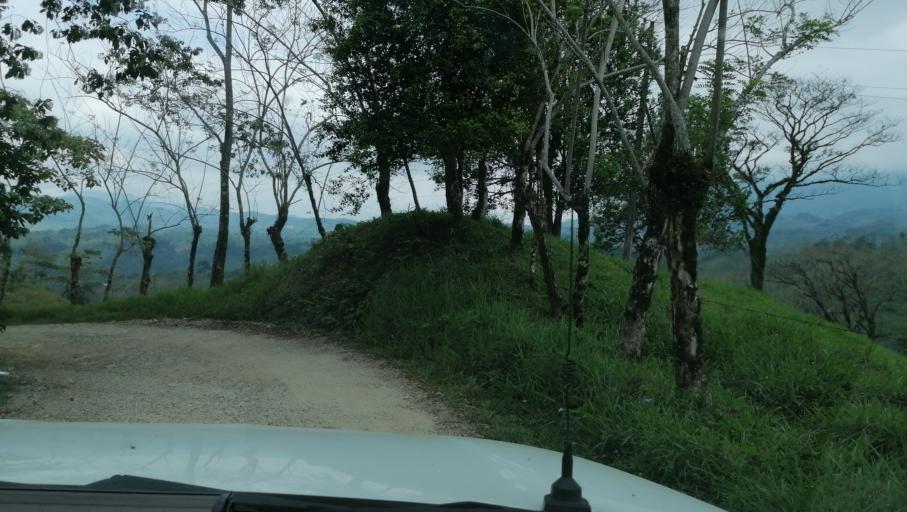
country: MX
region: Chiapas
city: Ocotepec
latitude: 17.2788
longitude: -93.2256
